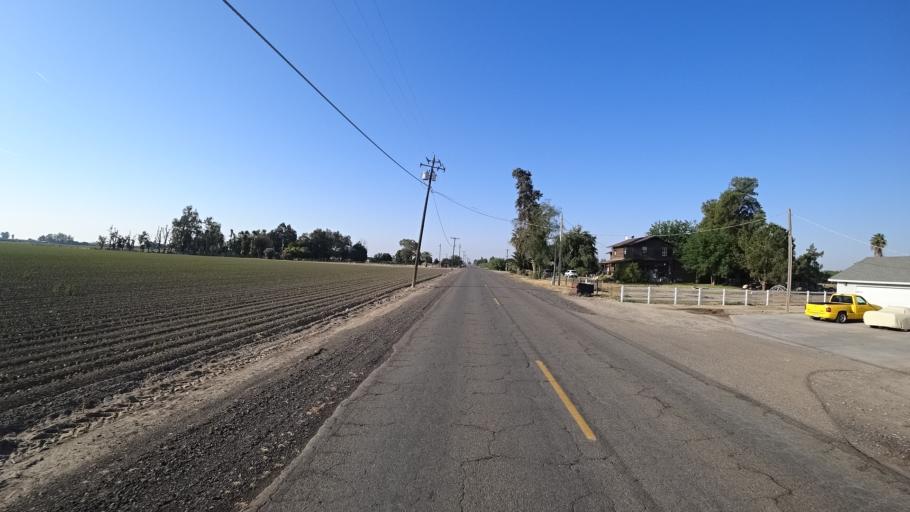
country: US
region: California
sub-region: Kings County
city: Lemoore
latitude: 36.2745
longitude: -119.7447
